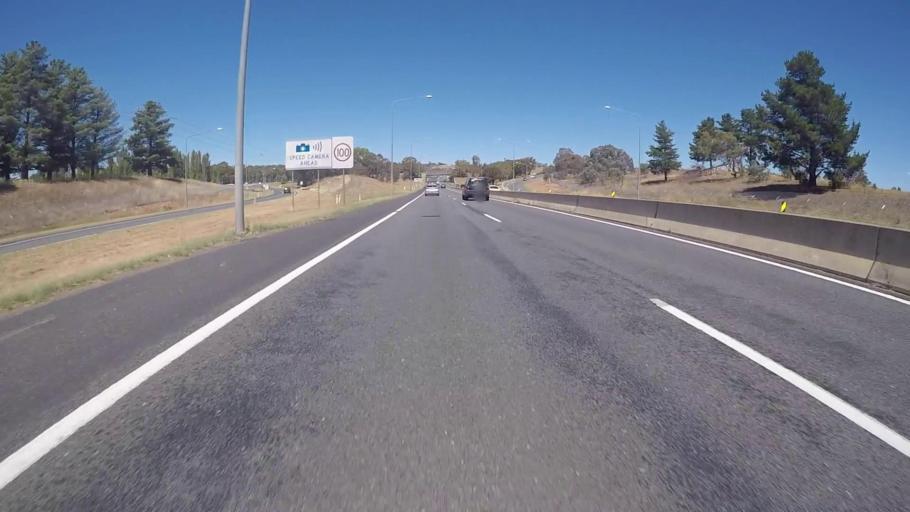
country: AU
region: Australian Capital Territory
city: Macquarie
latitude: -35.3167
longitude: 149.0631
